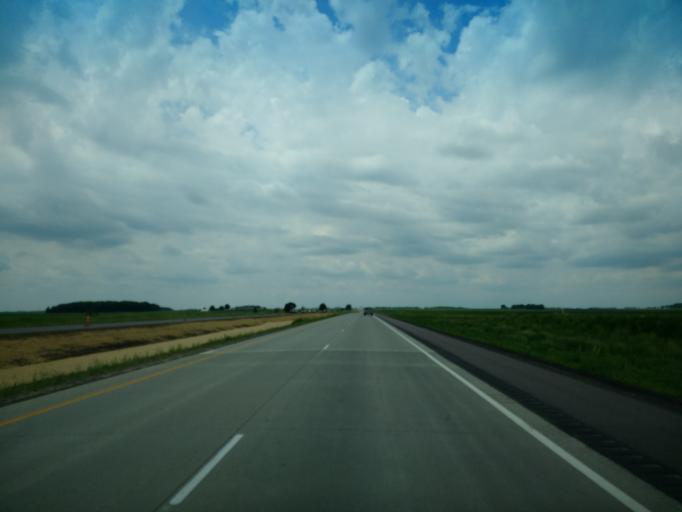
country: US
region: Minnesota
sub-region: Cottonwood County
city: Mountain Lake
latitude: 43.9273
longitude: -94.9678
